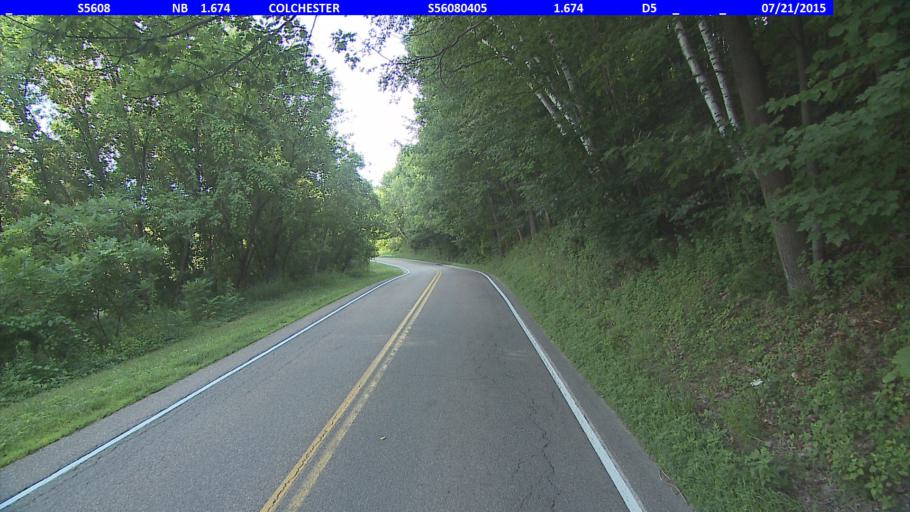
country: US
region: Vermont
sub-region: Chittenden County
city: Winooski
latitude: 44.5225
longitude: -73.2016
